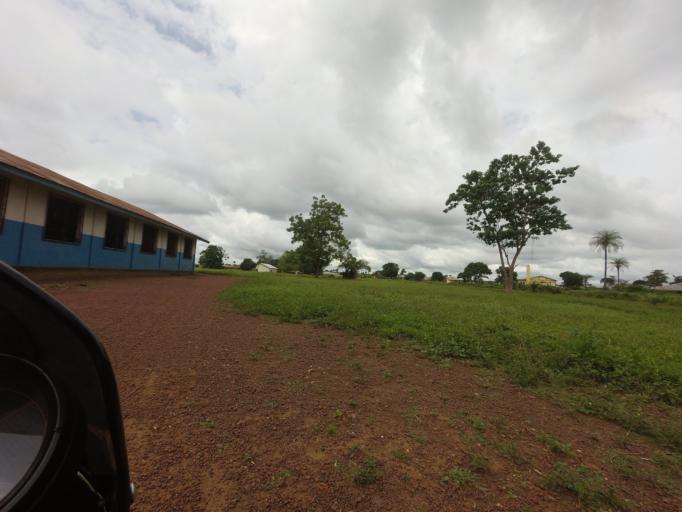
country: SL
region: Northern Province
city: Kukuna
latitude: 9.3893
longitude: -12.6692
